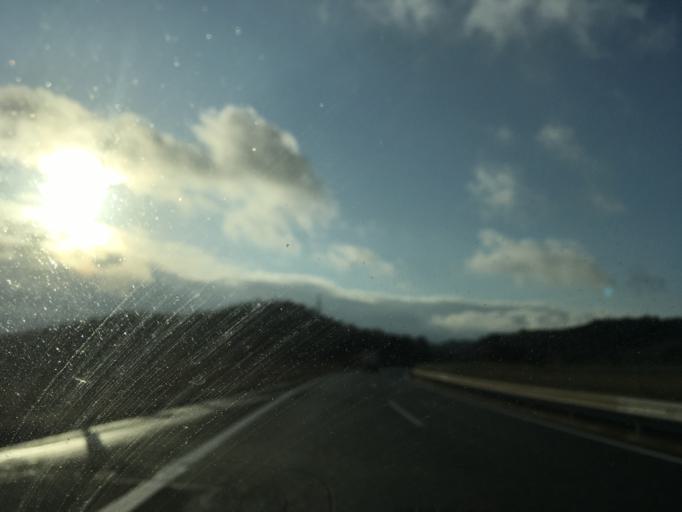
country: JP
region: Miyagi
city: Okawara
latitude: 38.1564
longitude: 140.6896
